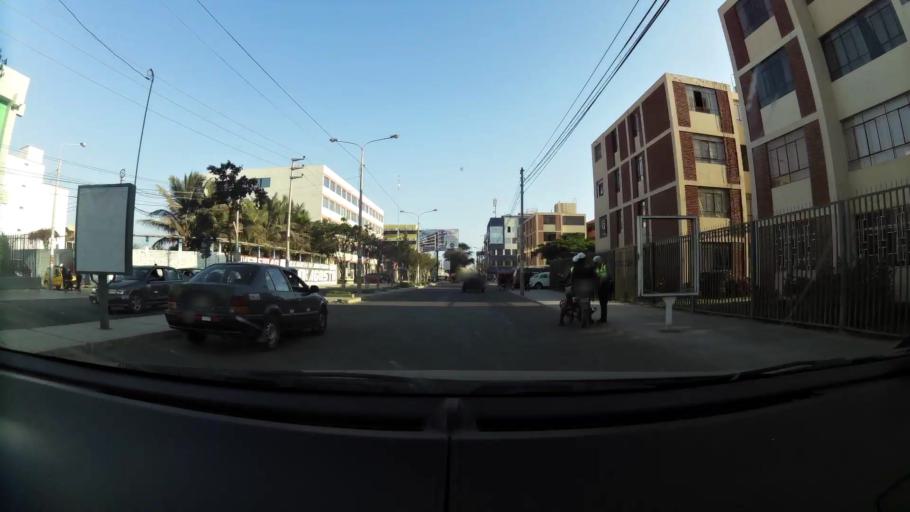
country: PE
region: Lambayeque
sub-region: Provincia de Chiclayo
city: Chiclayo
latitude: -6.7737
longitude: -79.8455
